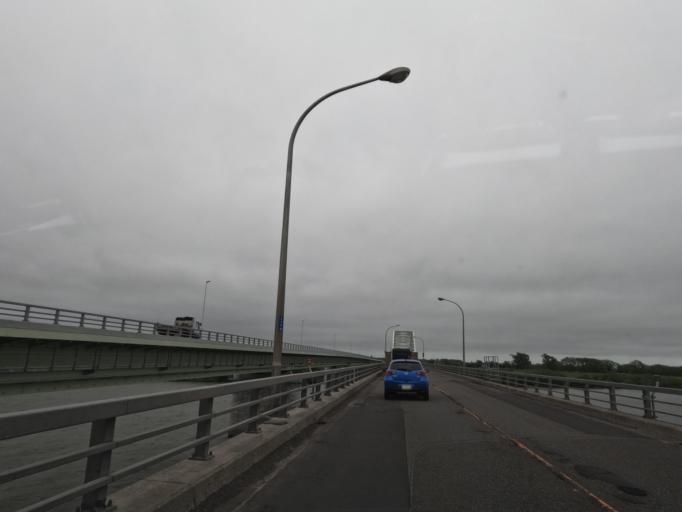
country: JP
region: Hokkaido
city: Ebetsu
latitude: 43.1345
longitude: 141.5104
